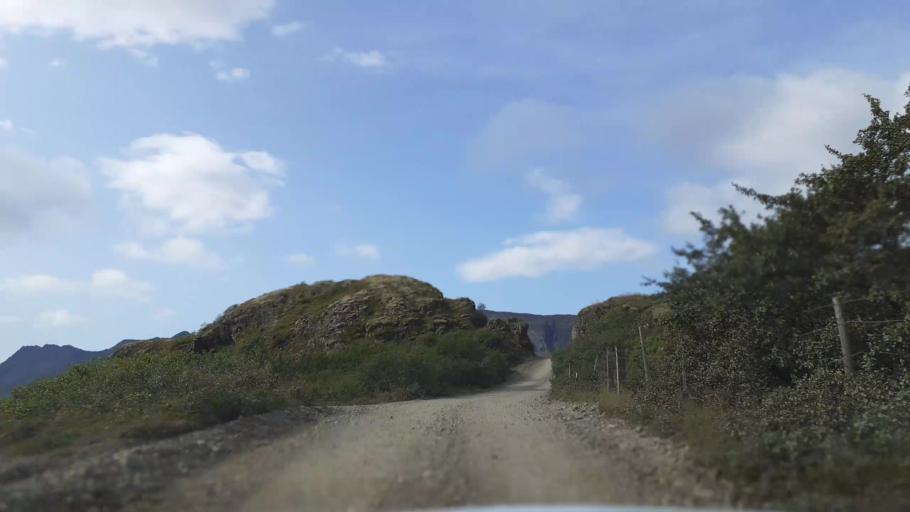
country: IS
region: East
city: Hoefn
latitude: 64.4364
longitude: -14.9046
